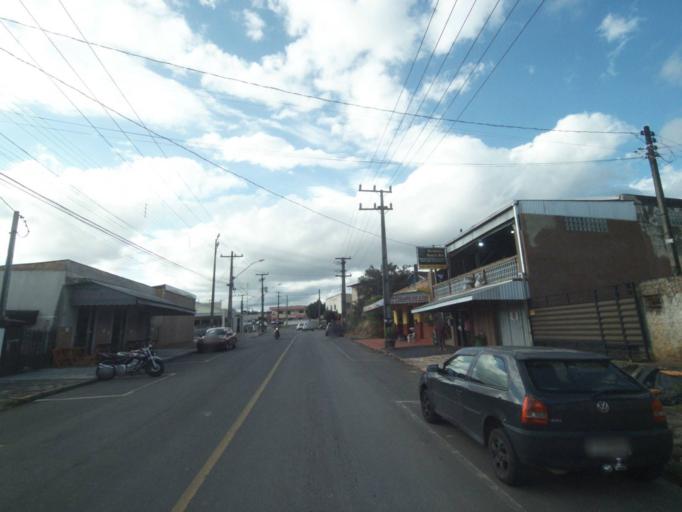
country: BR
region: Parana
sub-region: Telemaco Borba
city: Telemaco Borba
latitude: -24.3384
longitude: -50.6156
